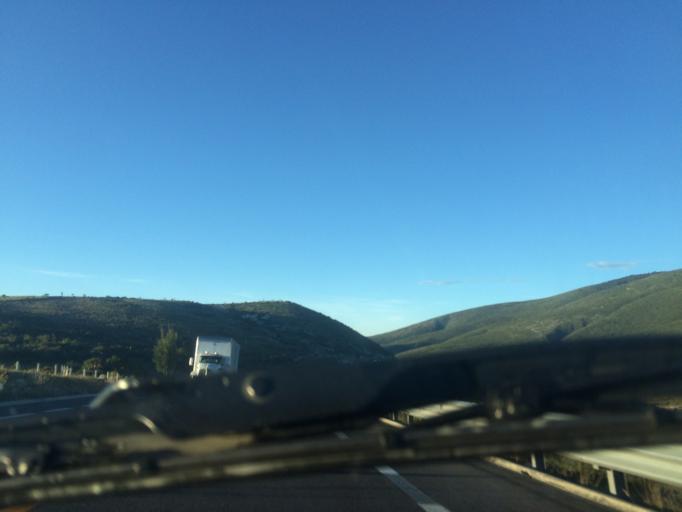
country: MX
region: Puebla
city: Morelos Canada
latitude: 18.6863
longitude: -97.4604
